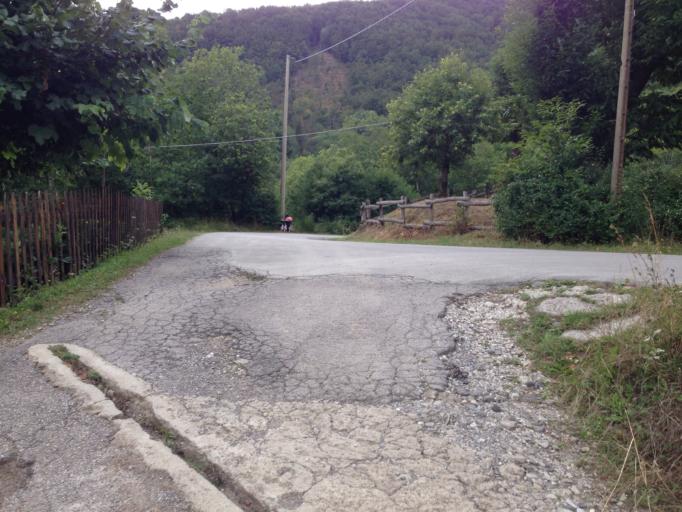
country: IT
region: Tuscany
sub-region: Provincia di Prato
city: Cantagallo
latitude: 44.0714
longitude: 11.0899
